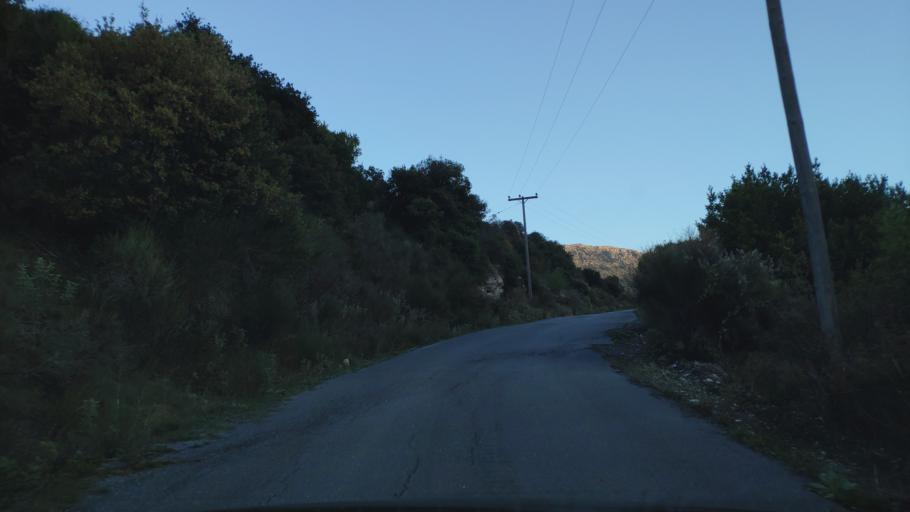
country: GR
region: Peloponnese
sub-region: Nomos Arkadias
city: Dimitsana
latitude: 37.5870
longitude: 22.0427
